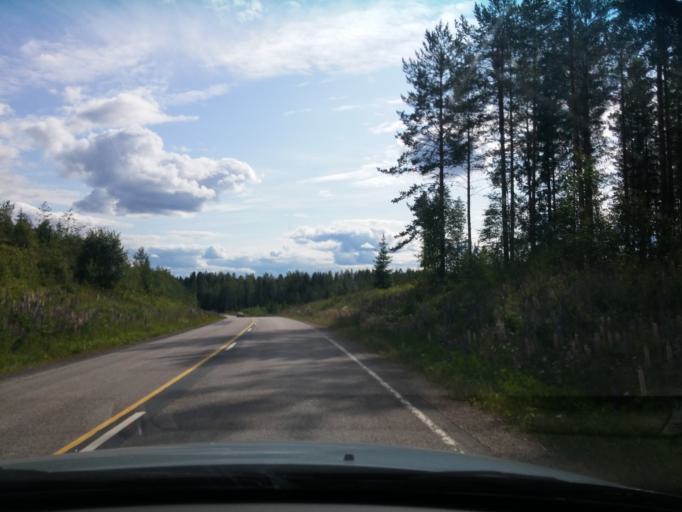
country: FI
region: Central Finland
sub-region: Keuruu
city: Keuruu
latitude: 62.3352
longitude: 24.7341
